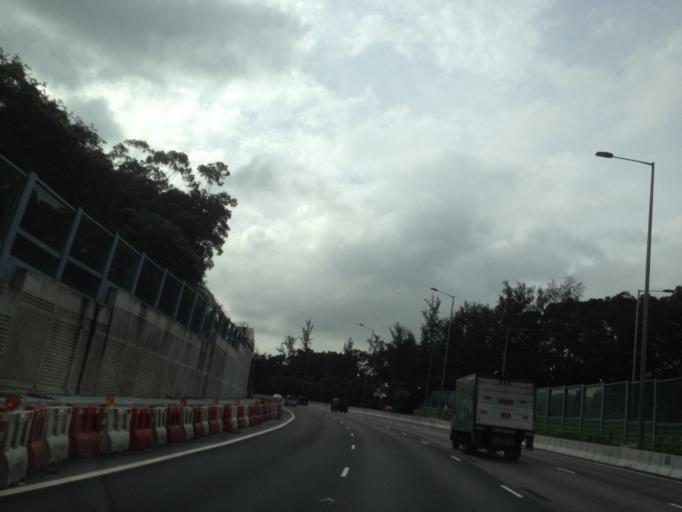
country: HK
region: Tai Po
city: Tai Po
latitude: 22.4437
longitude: 114.1583
